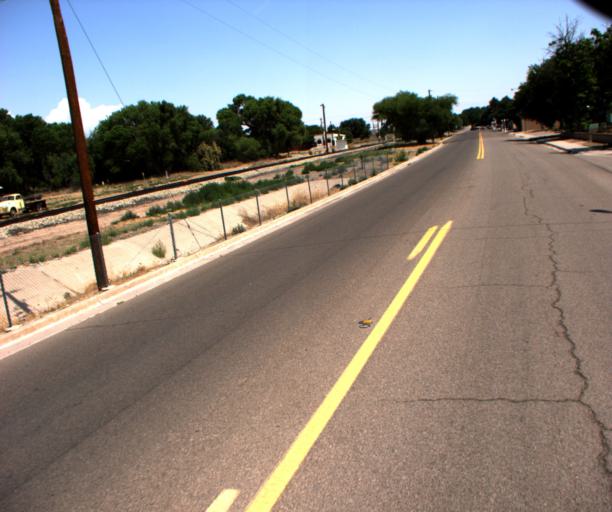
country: US
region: Arizona
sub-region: Greenlee County
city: Clifton
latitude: 32.7234
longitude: -109.1062
